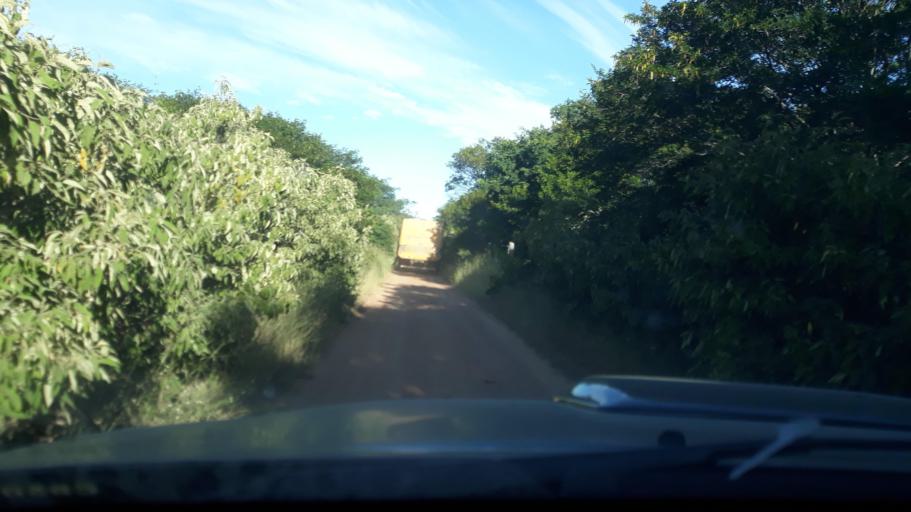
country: BR
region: Bahia
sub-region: Riacho De Santana
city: Riacho de Santana
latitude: -13.8576
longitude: -43.0422
